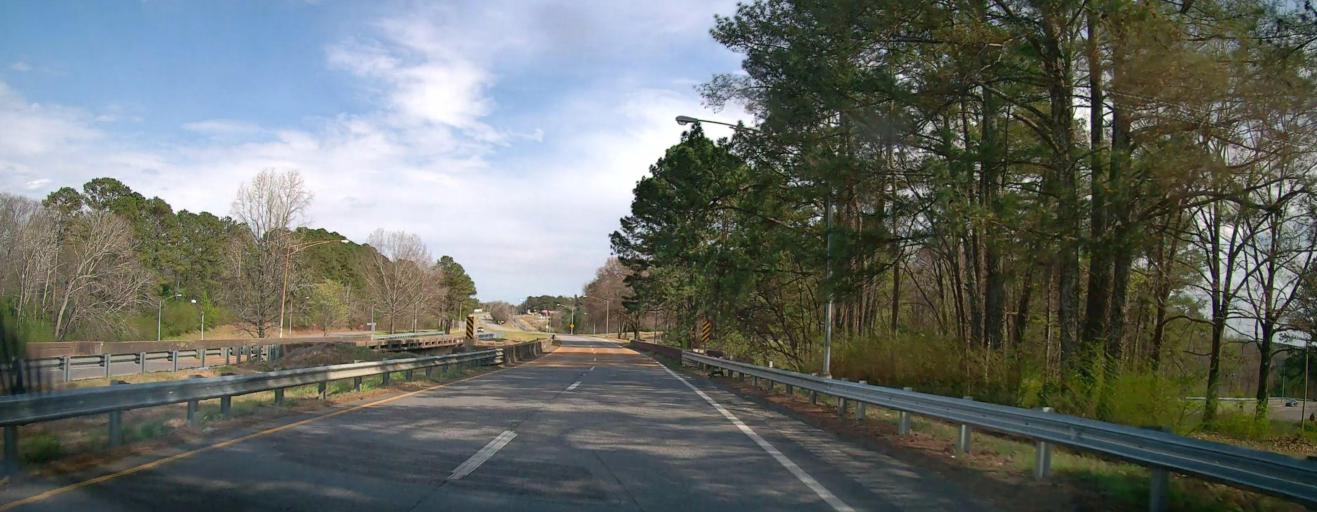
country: US
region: Alabama
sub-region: Jefferson County
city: Adamsville
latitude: 33.5857
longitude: -86.9325
